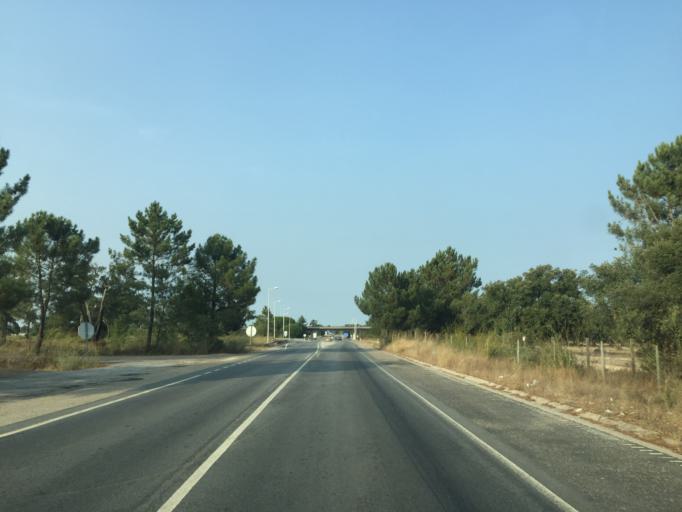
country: PT
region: Setubal
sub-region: Setubal
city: Setubal
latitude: 38.5921
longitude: -8.6745
